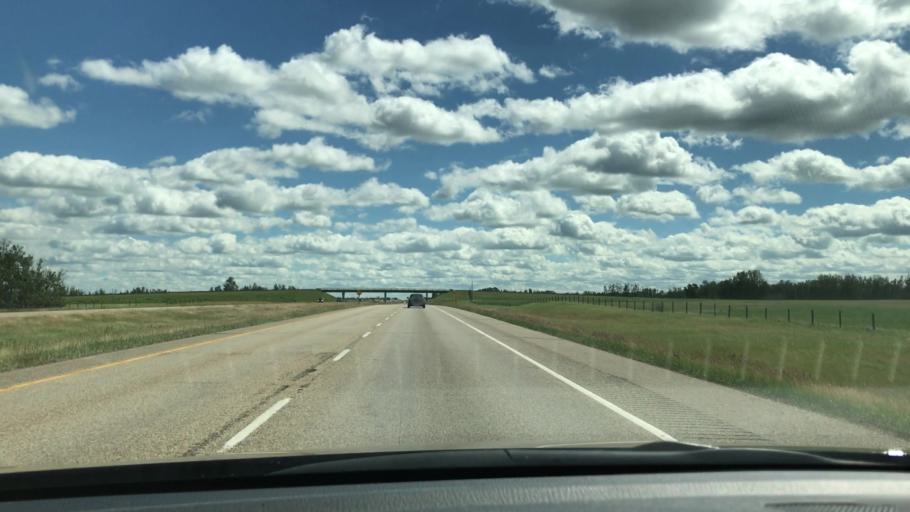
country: CA
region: Alberta
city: Millet
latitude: 53.1386
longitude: -113.5984
